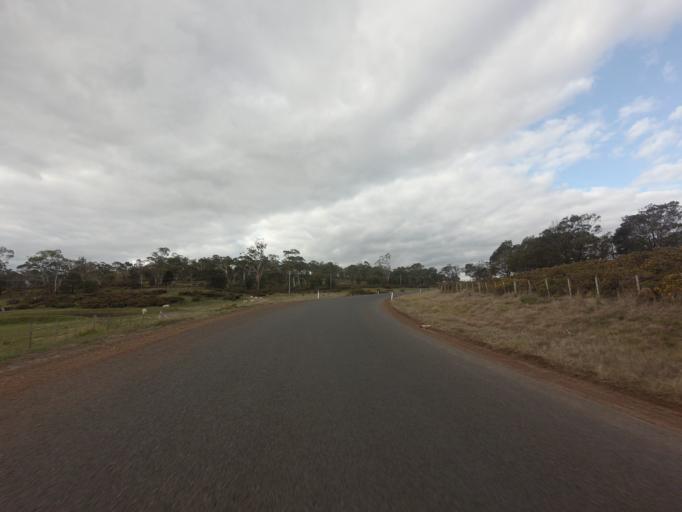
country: AU
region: Tasmania
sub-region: Northern Midlands
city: Evandale
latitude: -41.8964
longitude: 147.4074
